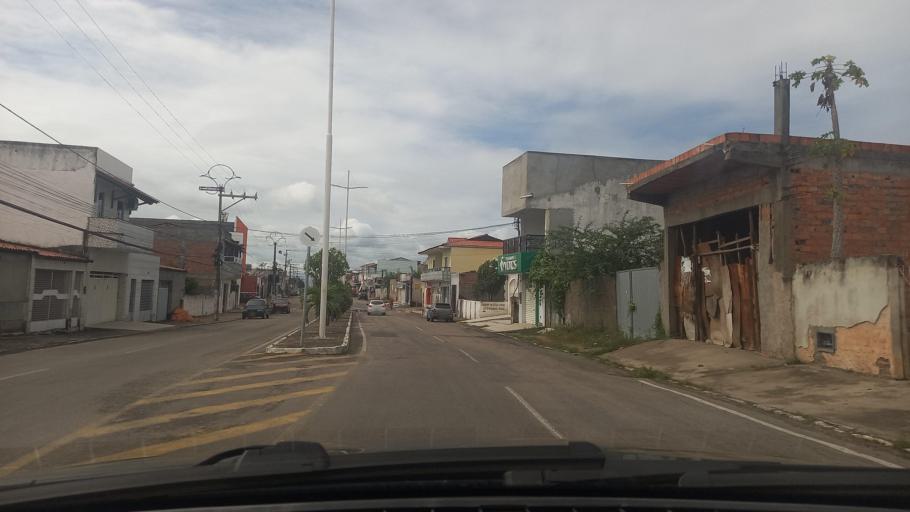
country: BR
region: Bahia
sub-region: Paulo Afonso
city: Paulo Afonso
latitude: -9.4426
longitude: -38.2151
